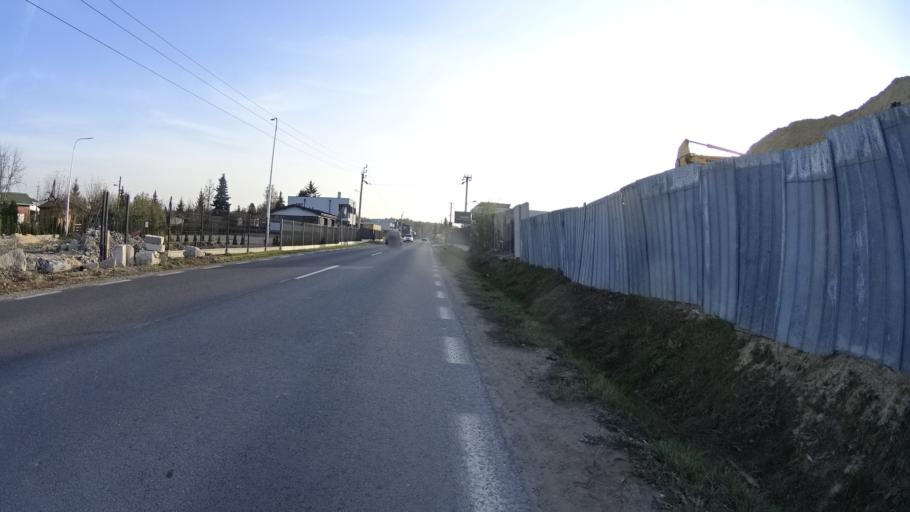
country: PL
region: Masovian Voivodeship
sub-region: Powiat warszawski zachodni
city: Babice
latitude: 52.2812
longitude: 20.8668
